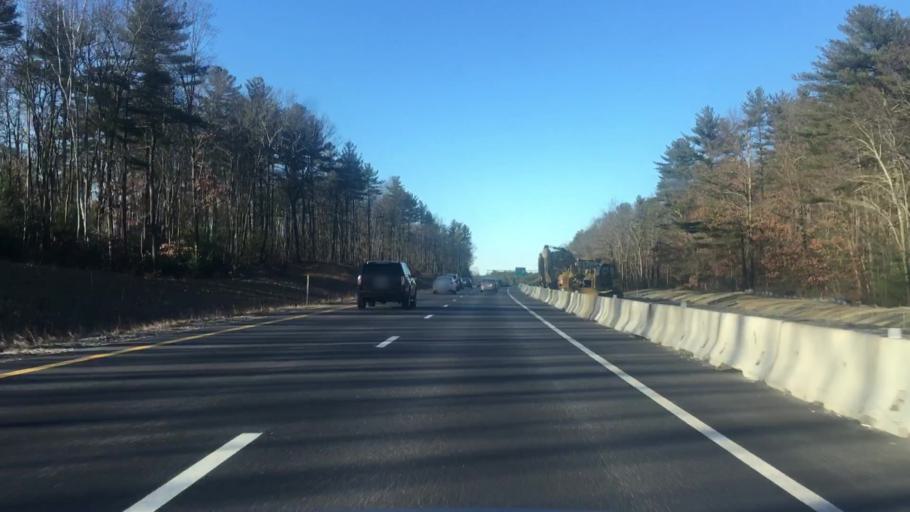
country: US
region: New Hampshire
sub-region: Rockingham County
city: Londonderry
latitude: 42.9290
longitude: -71.3793
